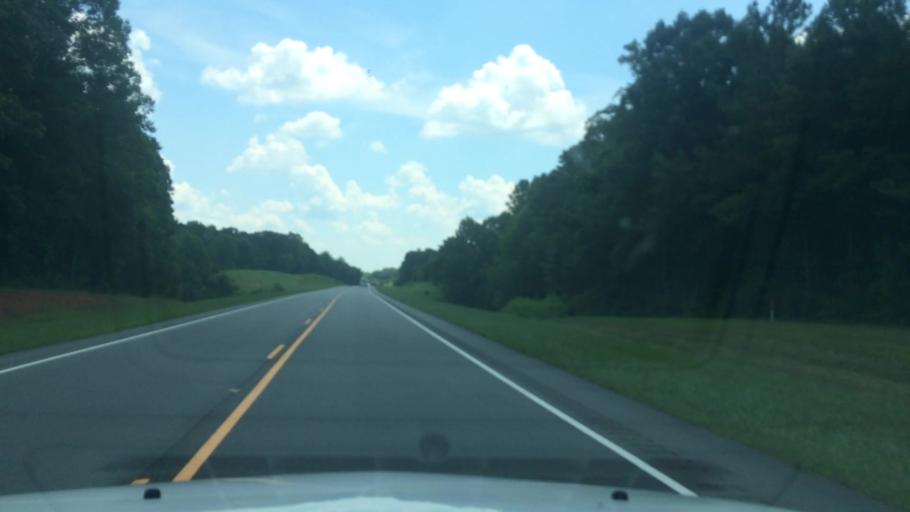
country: US
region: North Carolina
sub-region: Alexander County
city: Stony Point
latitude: 35.8733
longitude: -81.0666
